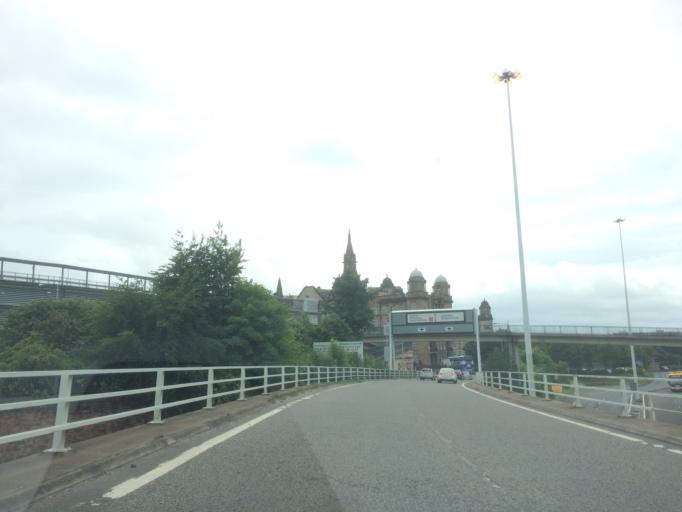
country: GB
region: Scotland
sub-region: Glasgow City
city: Glasgow
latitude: 55.8664
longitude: -4.2360
